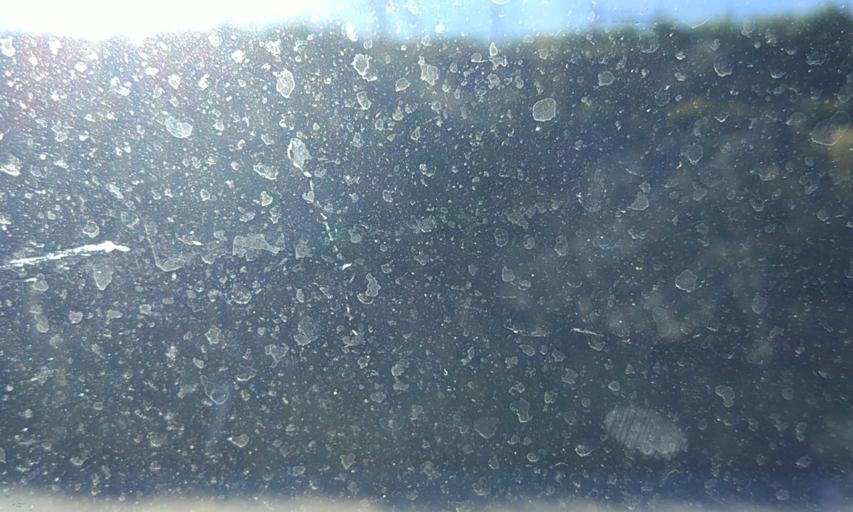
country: PT
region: Vila Real
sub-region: Sabrosa
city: Sabrosa
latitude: 41.3539
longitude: -7.5957
